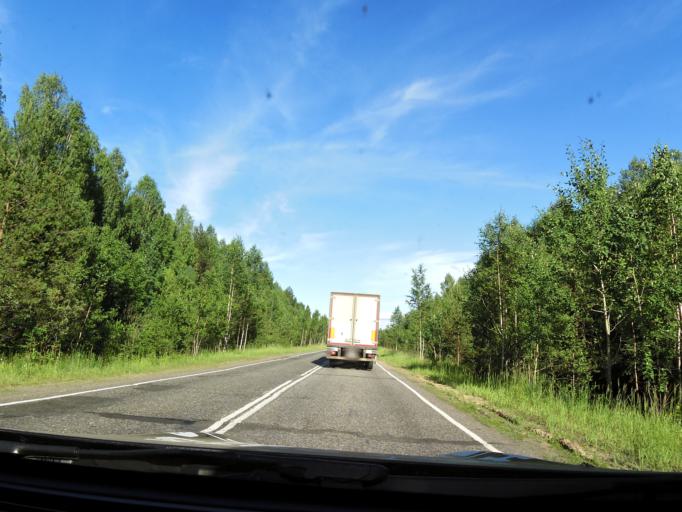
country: RU
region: Kirov
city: Chernaya Kholunitsa
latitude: 58.8765
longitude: 51.4772
